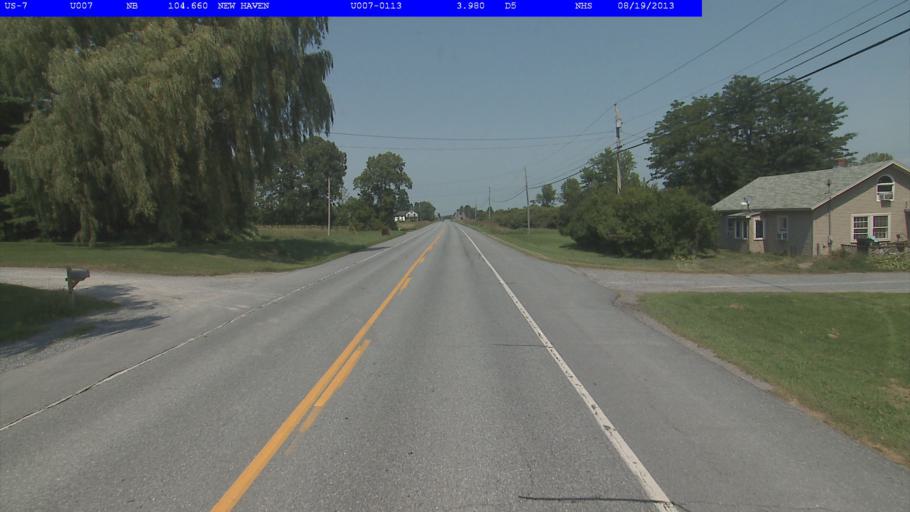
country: US
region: Vermont
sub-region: Addison County
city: Middlebury (village)
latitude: 44.1027
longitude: -73.1735
